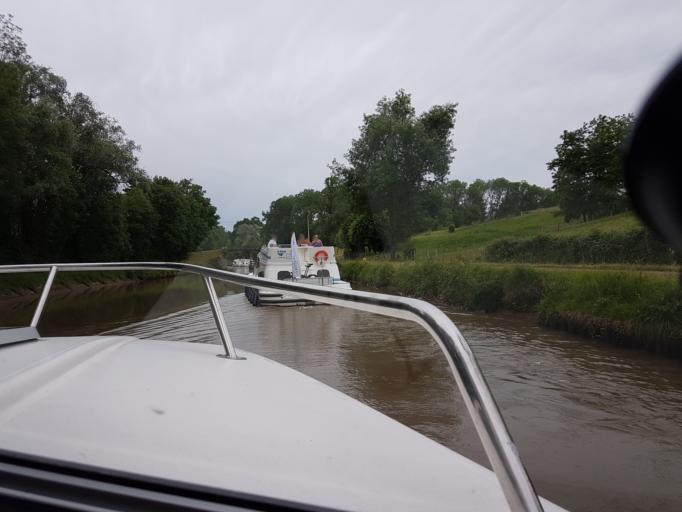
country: FR
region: Bourgogne
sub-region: Departement de la Nievre
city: Clamecy
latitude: 47.3983
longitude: 3.6028
